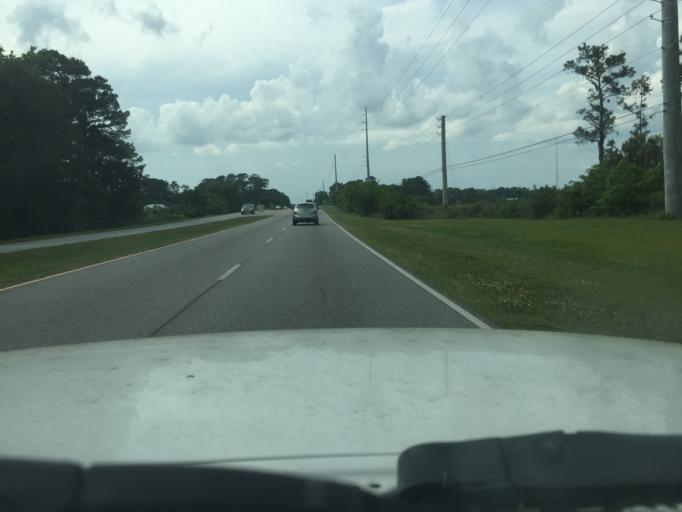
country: US
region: Georgia
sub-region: Chatham County
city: Whitemarsh Island
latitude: 32.0493
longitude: -81.0103
